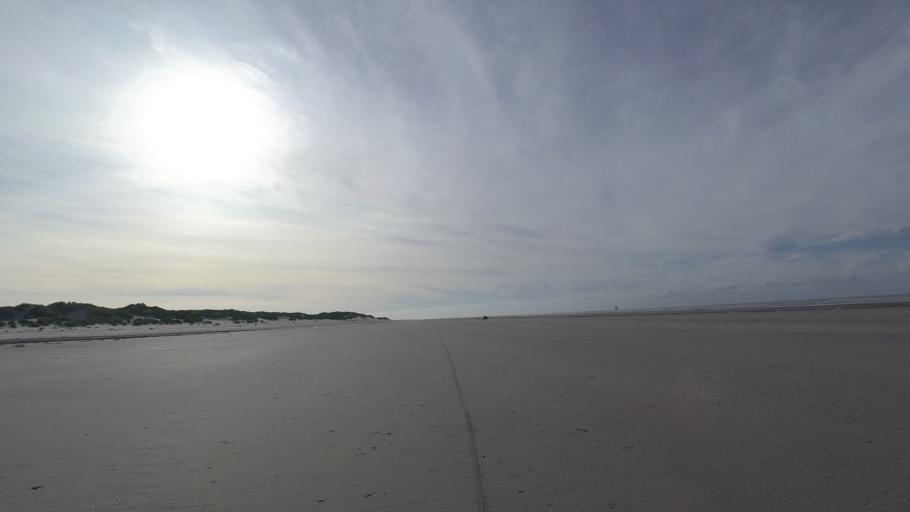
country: NL
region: Friesland
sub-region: Gemeente Dongeradeel
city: Ternaard
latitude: 53.4680
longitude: 5.9233
